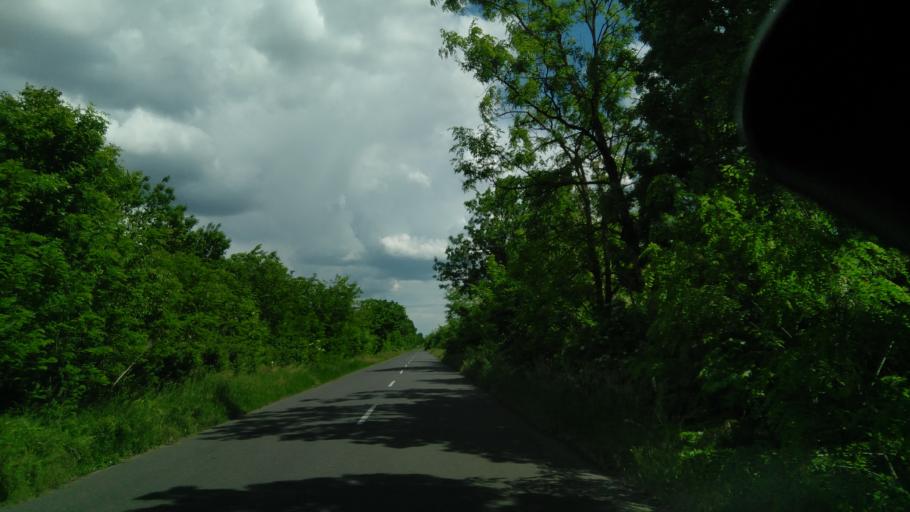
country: HU
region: Bekes
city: Korosladany
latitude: 46.9808
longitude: 21.0495
